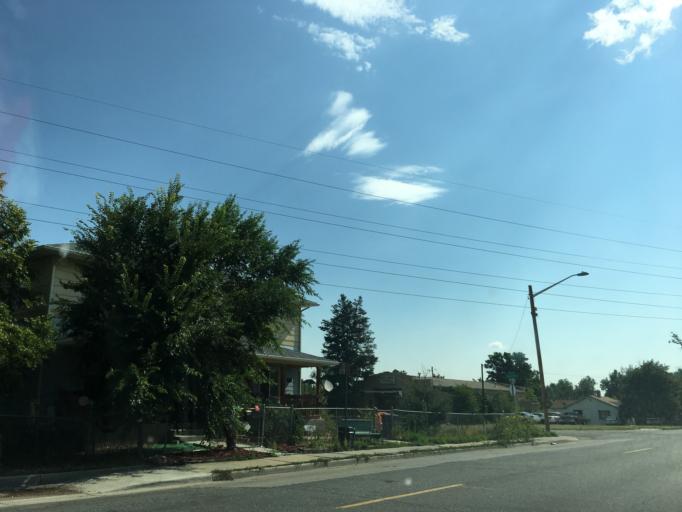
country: US
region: Colorado
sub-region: Jefferson County
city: Lakewood
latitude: 39.7003
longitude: -105.0414
